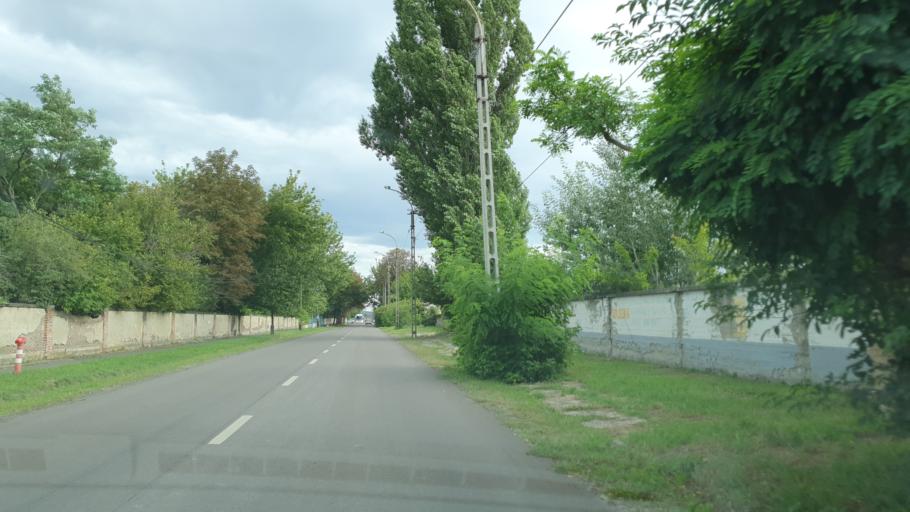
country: HU
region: Heves
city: Zagyvaszanto
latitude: 47.7653
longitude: 19.6723
